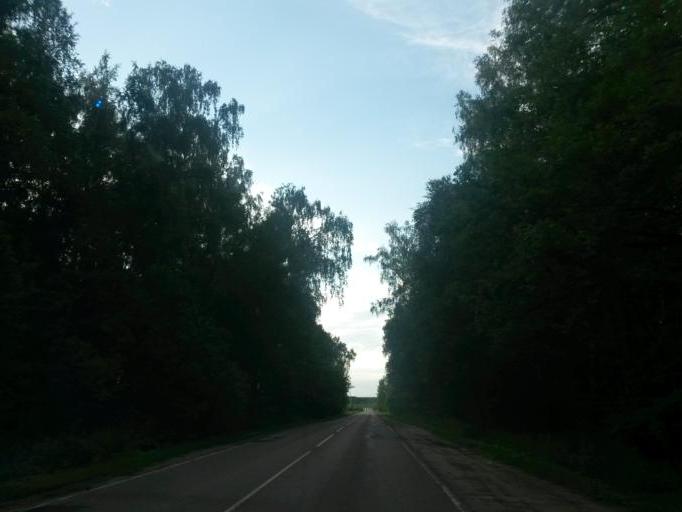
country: RU
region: Moskovskaya
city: Melikhovo
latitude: 55.1878
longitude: 37.7029
